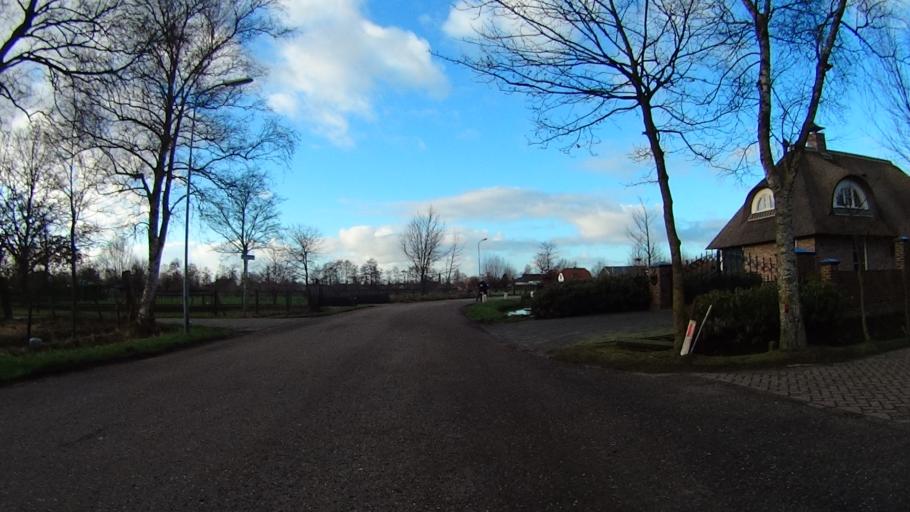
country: NL
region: Gelderland
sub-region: Gemeente Barneveld
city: Zwartebroek
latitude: 52.1899
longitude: 5.4745
